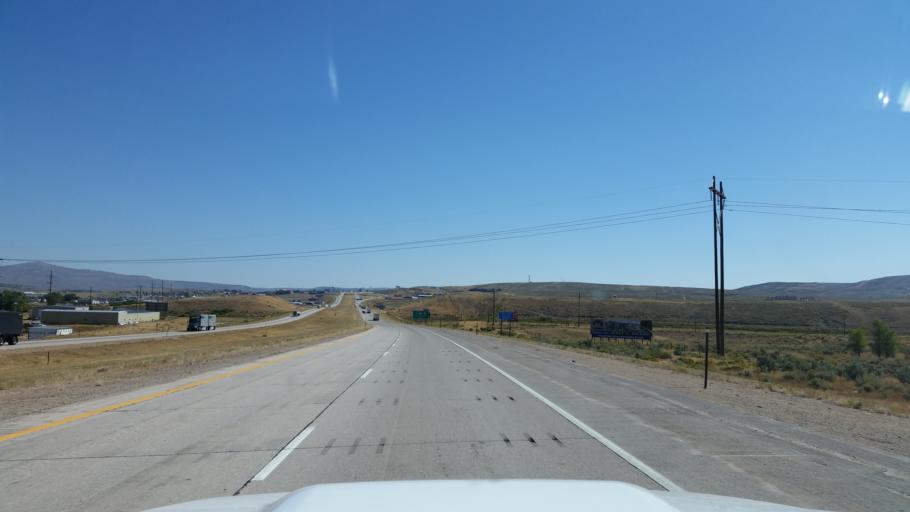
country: US
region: Wyoming
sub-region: Uinta County
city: Evanston
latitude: 41.2488
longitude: -111.0113
